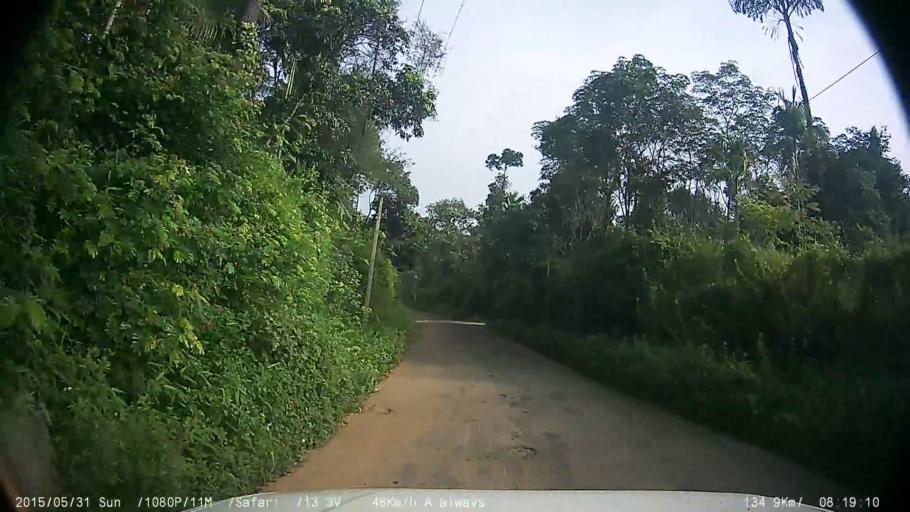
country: IN
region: Kerala
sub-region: Wayanad
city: Kalpetta
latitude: 11.6683
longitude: 75.9842
